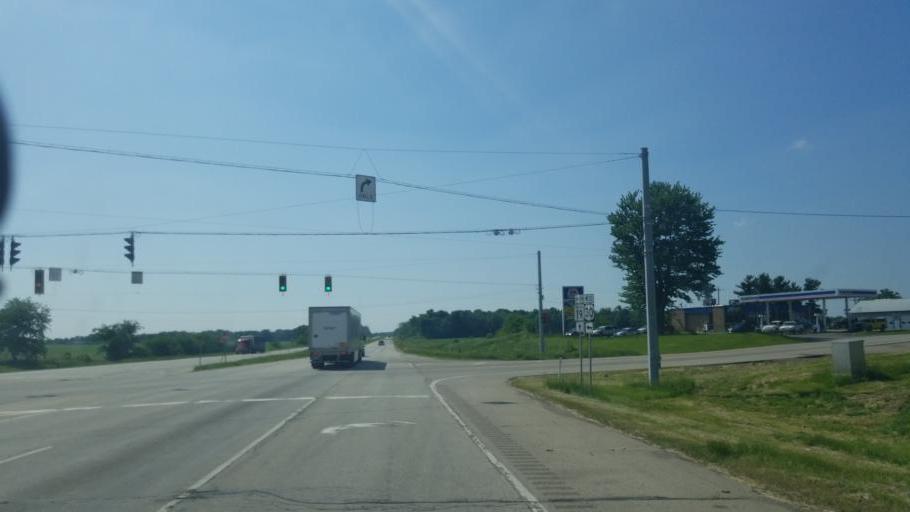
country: US
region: Indiana
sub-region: Marshall County
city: Bourbon
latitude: 41.2822
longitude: -86.0465
